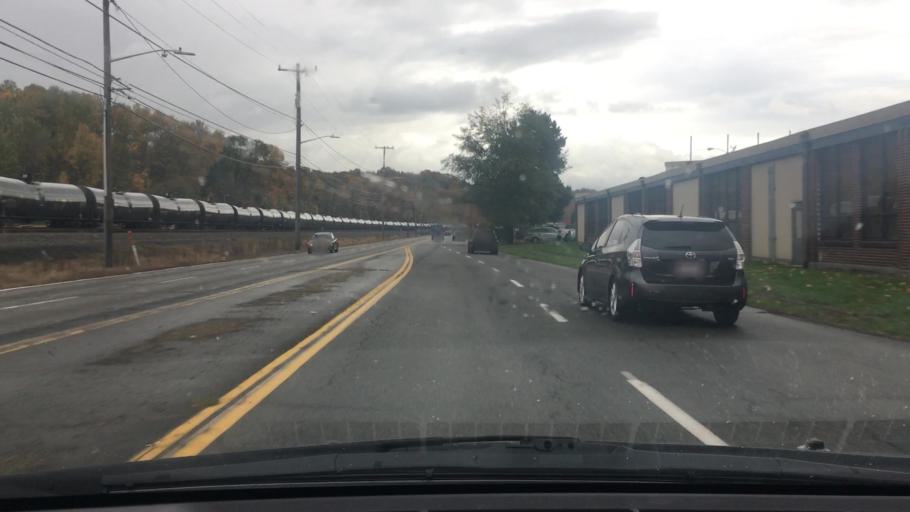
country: US
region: Washington
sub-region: King County
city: Boulevard Park
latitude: 47.5369
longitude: -122.3019
